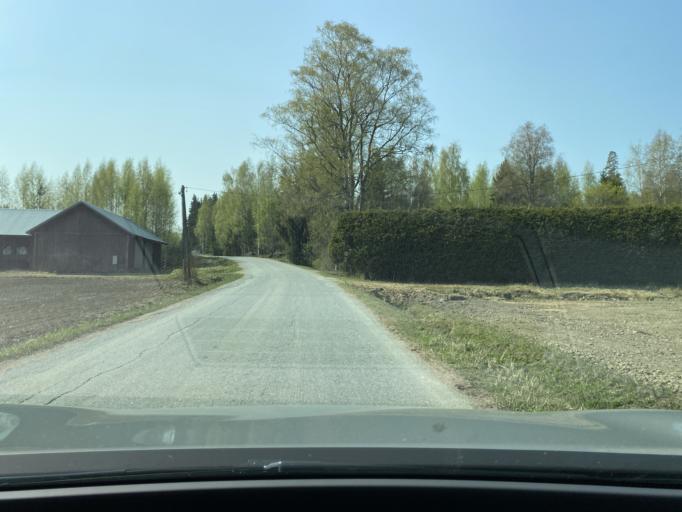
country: FI
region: Satakunta
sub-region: Pori
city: Huittinen
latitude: 61.1283
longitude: 22.8121
